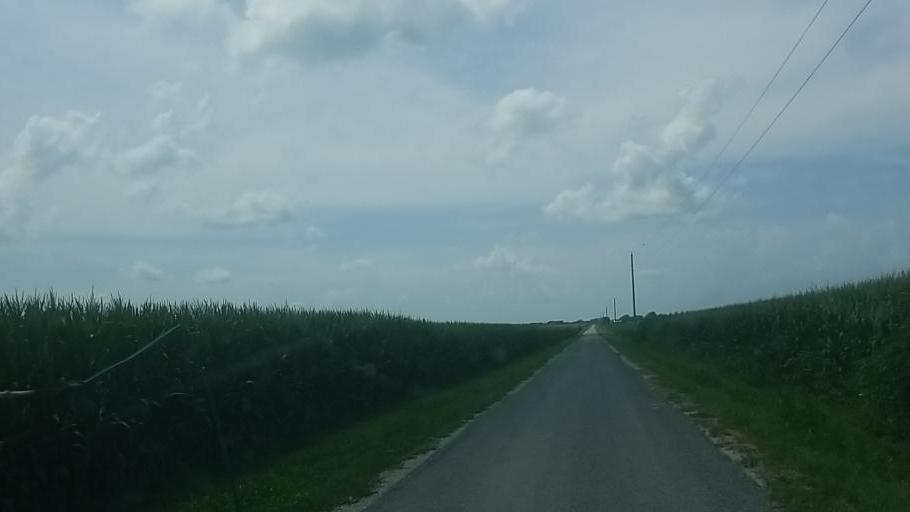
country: US
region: Ohio
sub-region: Wyandot County
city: Upper Sandusky
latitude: 40.6732
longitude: -83.2734
